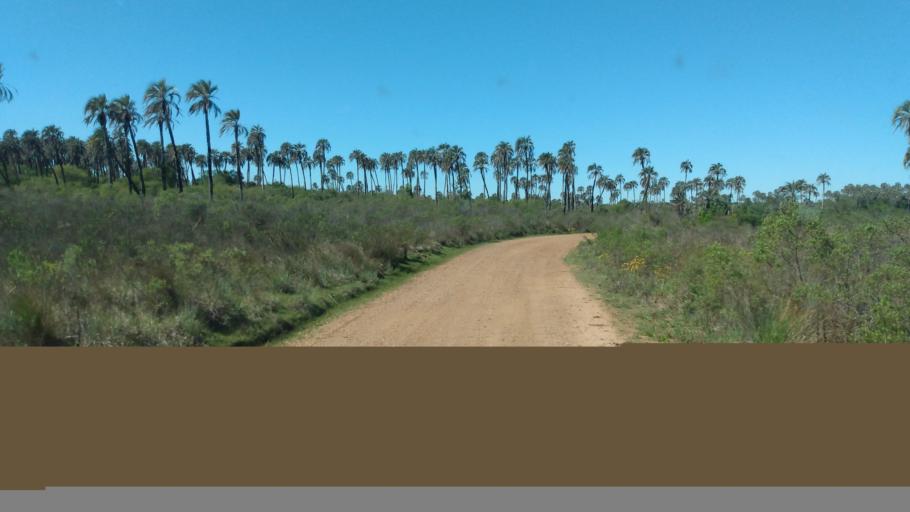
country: AR
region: Entre Rios
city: Ubajay
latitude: -31.8840
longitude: -58.2368
